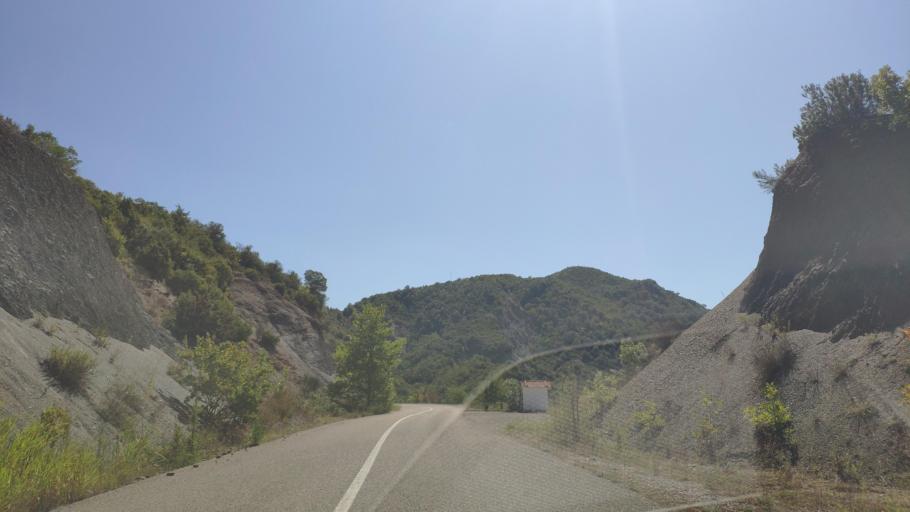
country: GR
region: Central Greece
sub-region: Nomos Evrytanias
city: Kerasochori
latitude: 39.0069
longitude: 21.5295
